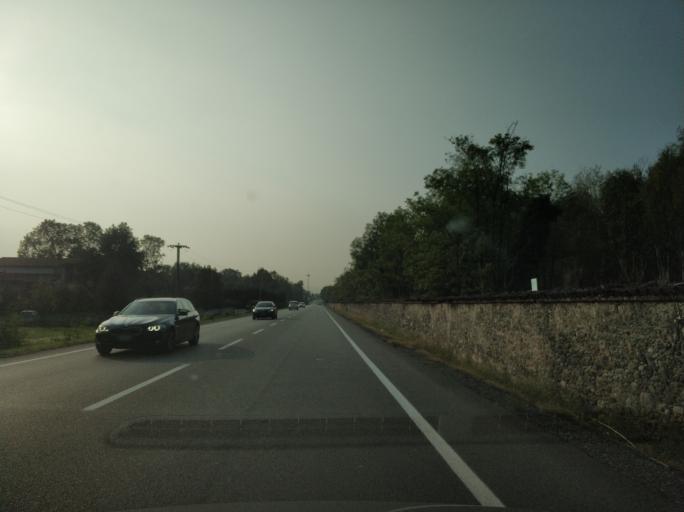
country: IT
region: Piedmont
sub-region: Provincia di Torino
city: Robassomero
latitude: 45.1980
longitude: 7.5588
